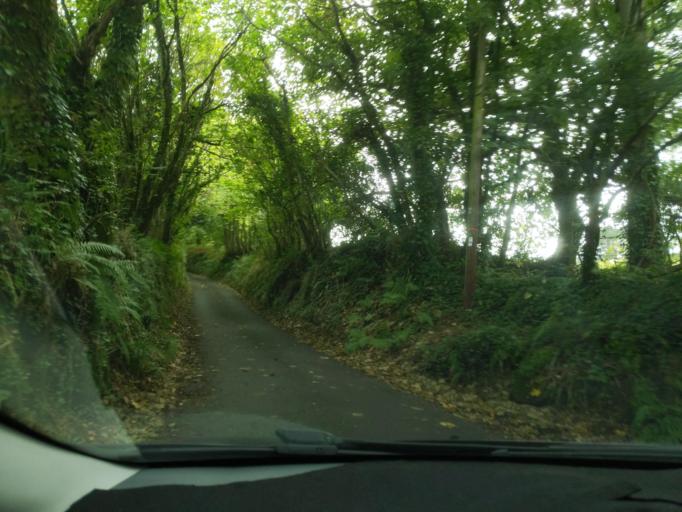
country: GB
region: England
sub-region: Cornwall
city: Lostwithiel
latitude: 50.3952
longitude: -4.7040
